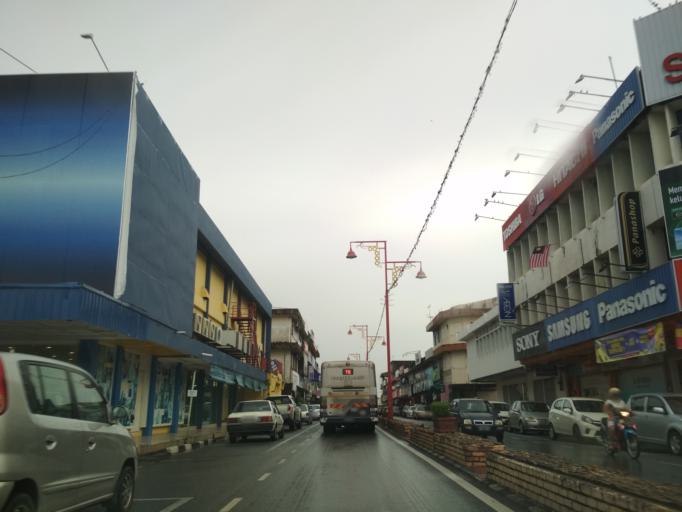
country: MY
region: Perlis
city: Kangar
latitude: 6.4362
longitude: 100.1911
